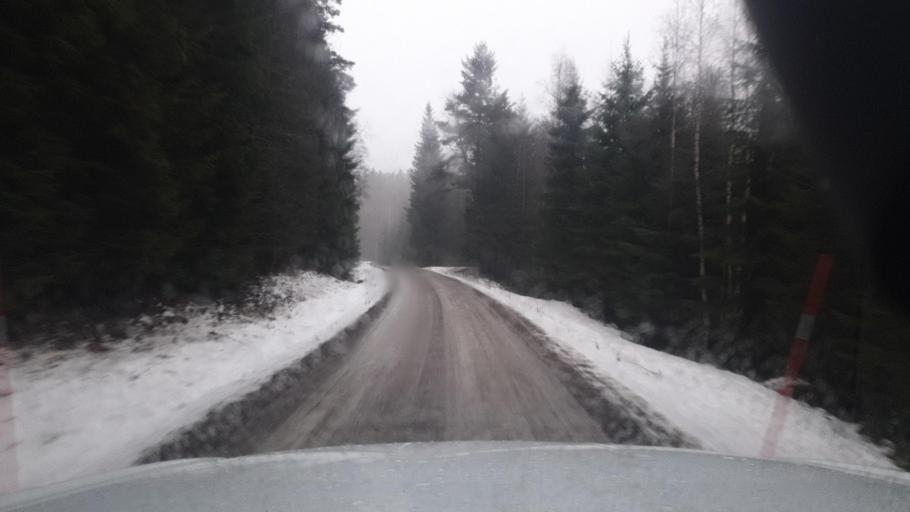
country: SE
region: Vaermland
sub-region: Eda Kommun
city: Charlottenberg
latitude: 60.0225
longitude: 12.6318
